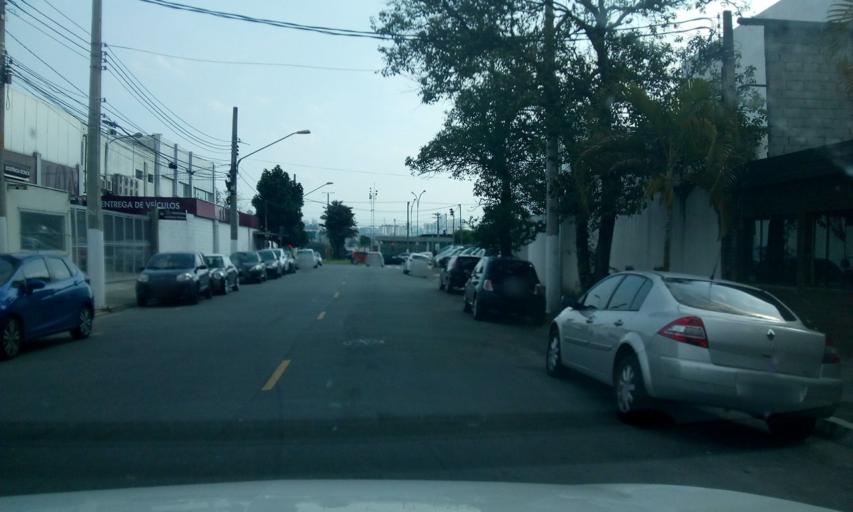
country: BR
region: Sao Paulo
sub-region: Osasco
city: Osasco
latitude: -23.5312
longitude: -46.7356
